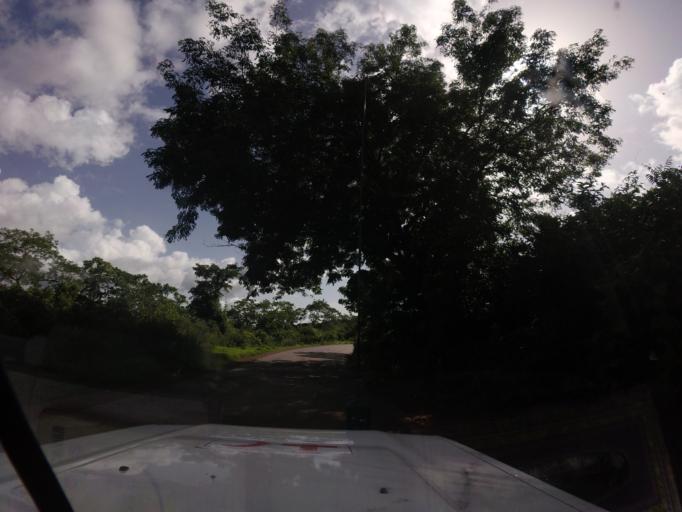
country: GN
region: Mamou
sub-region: Mamou Prefecture
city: Mamou
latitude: 10.2974
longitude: -12.3260
